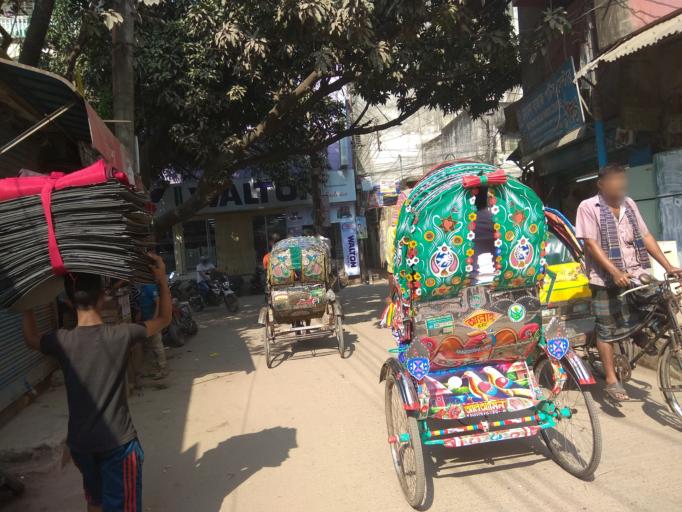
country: BD
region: Dhaka
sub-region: Dhaka
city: Dhaka
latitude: 23.7196
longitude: 90.4037
